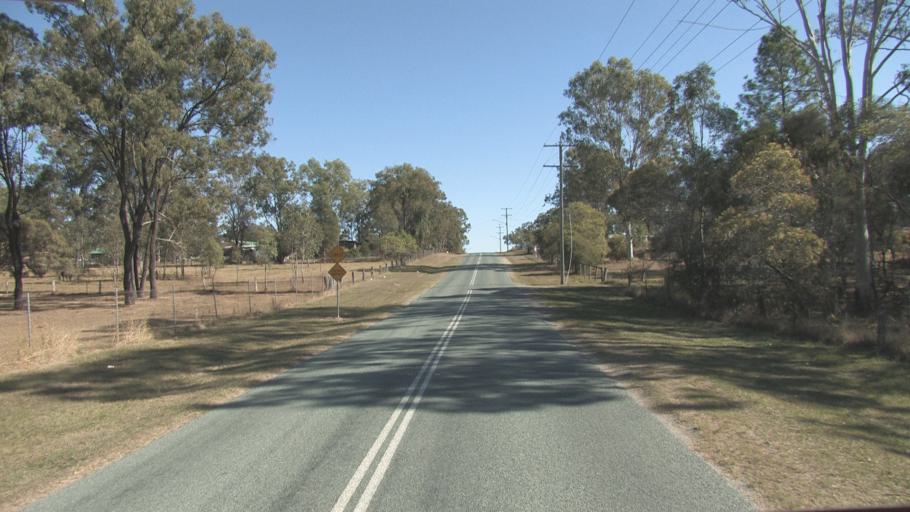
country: AU
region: Queensland
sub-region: Logan
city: Cedar Vale
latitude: -27.8490
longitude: 153.0314
